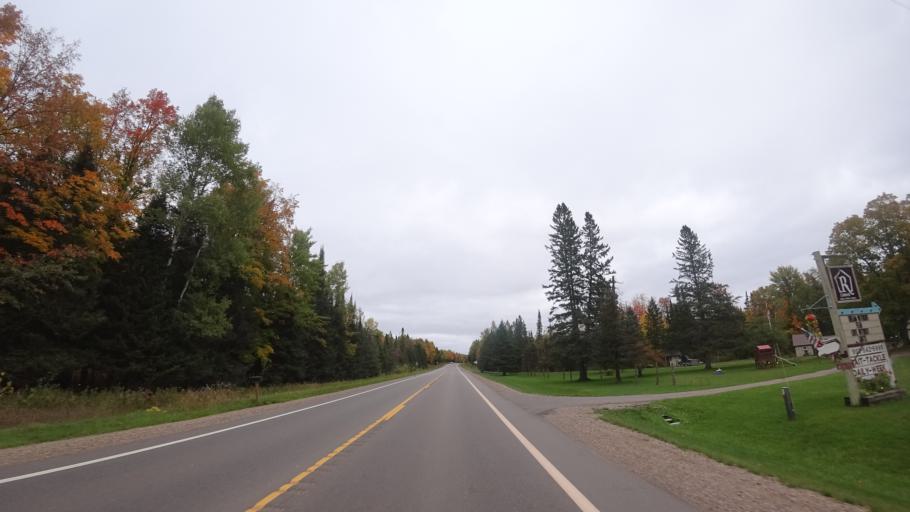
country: US
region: Michigan
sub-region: Iron County
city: Crystal Falls
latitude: 46.1621
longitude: -88.0778
